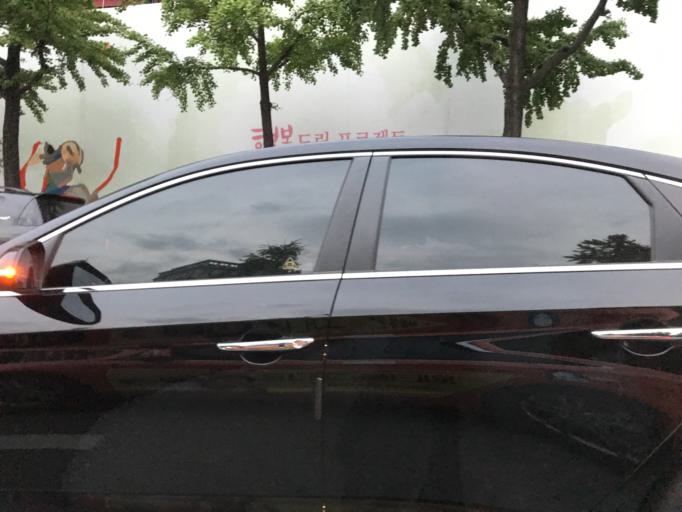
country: KR
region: Seoul
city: Seoul
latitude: 37.5746
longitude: 126.9830
